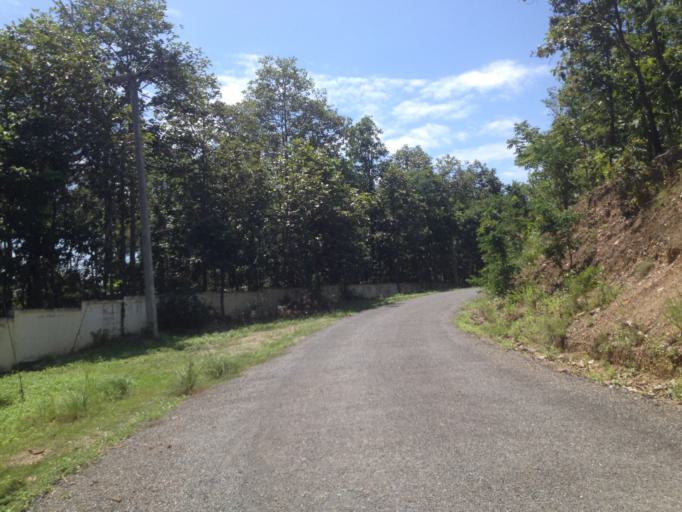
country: TH
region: Chiang Mai
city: Hang Dong
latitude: 18.7329
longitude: 98.9135
